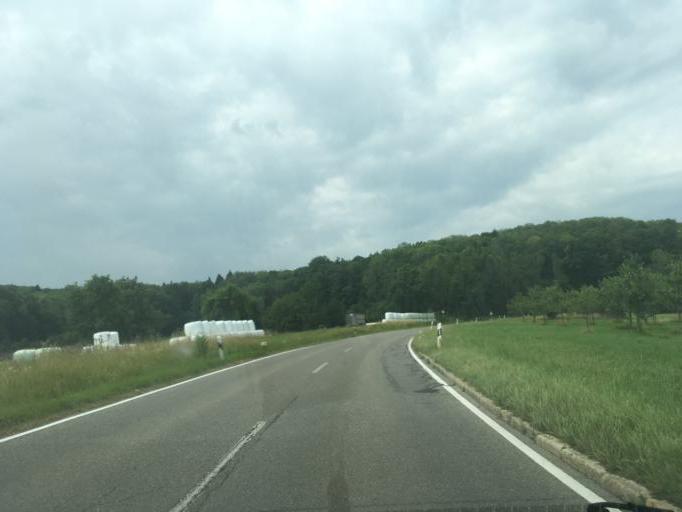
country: DE
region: Baden-Wuerttemberg
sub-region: Regierungsbezirk Stuttgart
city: Waldenbuch
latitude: 48.6259
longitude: 9.1313
